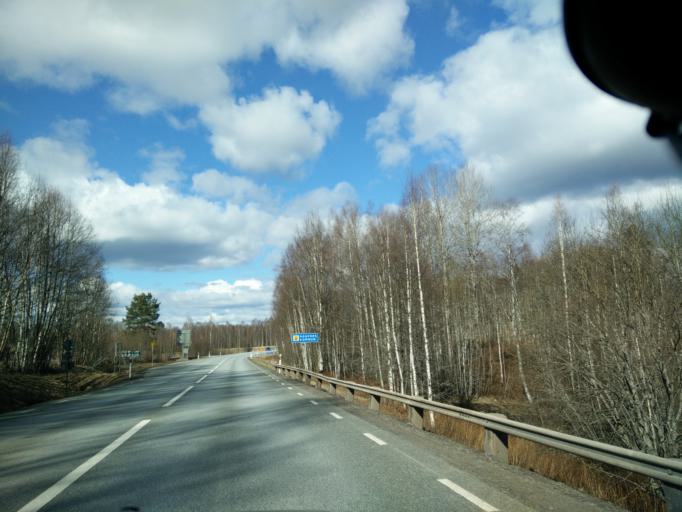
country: SE
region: Vaermland
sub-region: Munkfors Kommun
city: Munkfors
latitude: 59.8595
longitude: 13.5616
